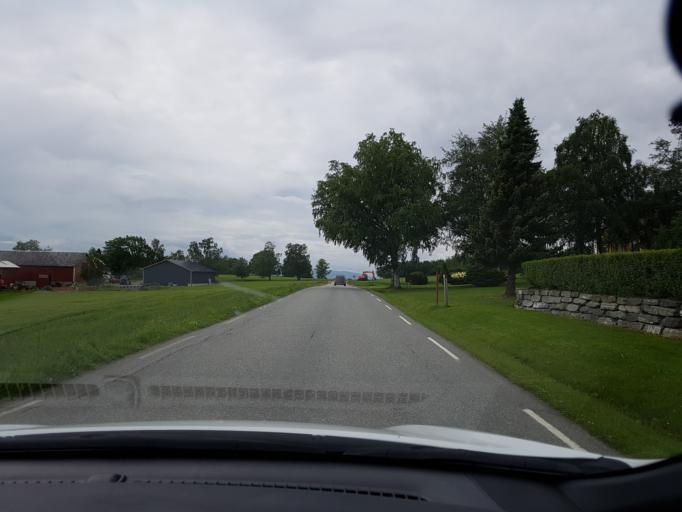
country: NO
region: Nord-Trondelag
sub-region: Frosta
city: Frosta
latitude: 63.5832
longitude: 10.7291
